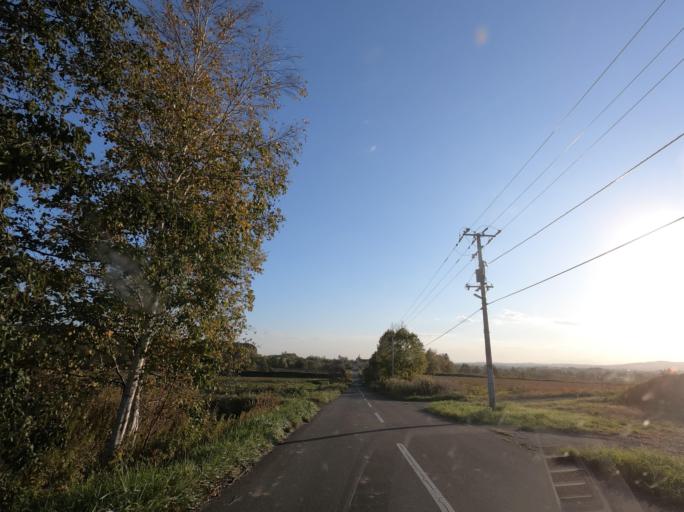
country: JP
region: Hokkaido
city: Iwamizawa
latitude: 43.0086
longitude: 141.8802
